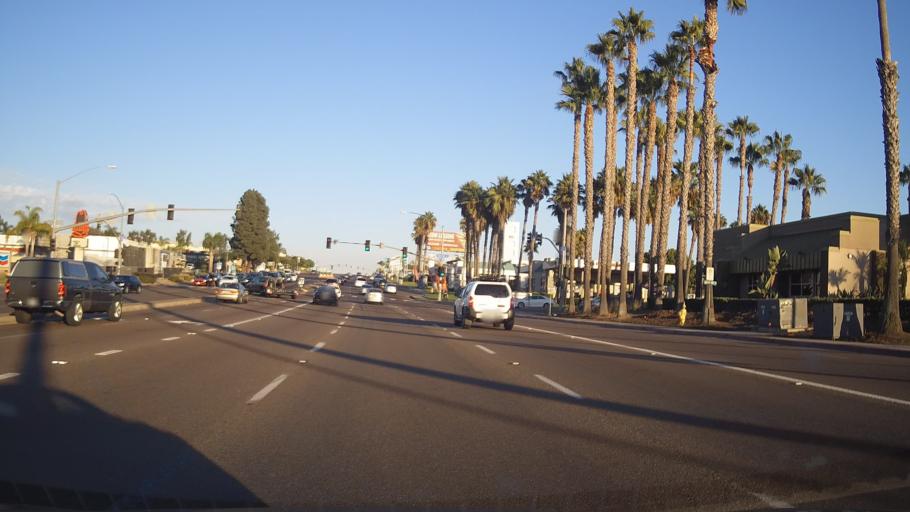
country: US
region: California
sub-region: San Diego County
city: La Jolla
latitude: 32.8326
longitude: -117.1647
